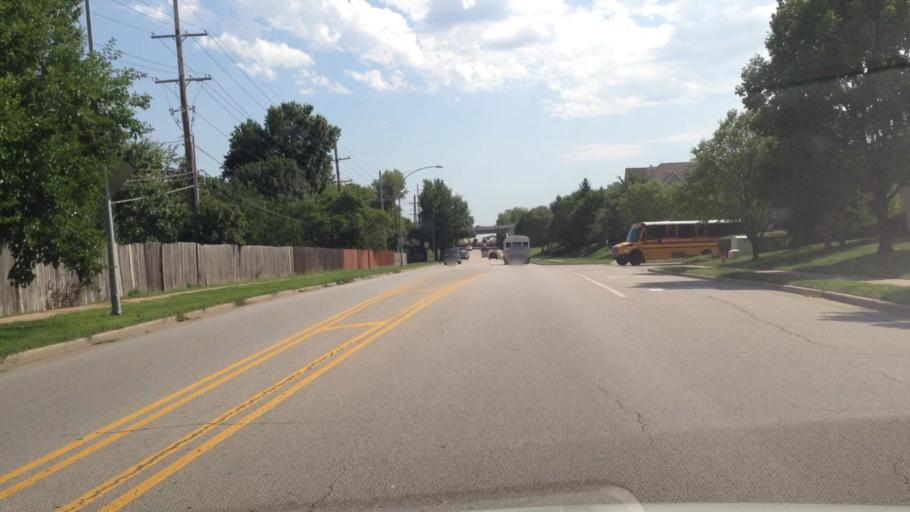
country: US
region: Kansas
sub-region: Johnson County
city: Lenexa
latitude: 38.9402
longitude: -94.7422
